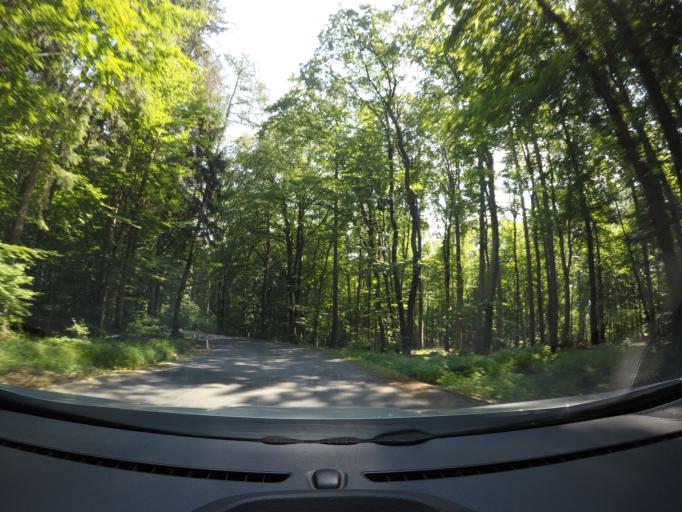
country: AT
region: Lower Austria
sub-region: Politischer Bezirk Wien-Umgebung
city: Mauerbach
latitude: 48.2686
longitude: 16.1619
